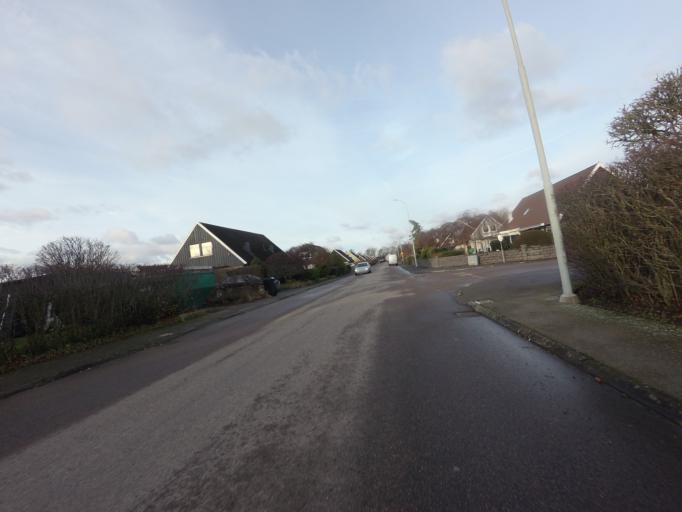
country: SE
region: Skane
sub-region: Hoganas Kommun
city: Hoganas
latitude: 56.1906
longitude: 12.5849
